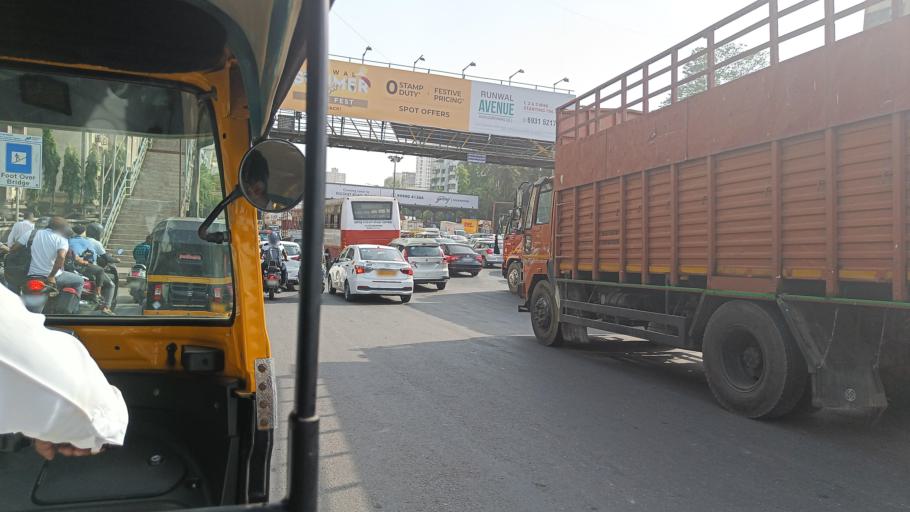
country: IN
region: Maharashtra
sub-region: Thane
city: Thane
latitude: 19.1700
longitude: 72.9677
